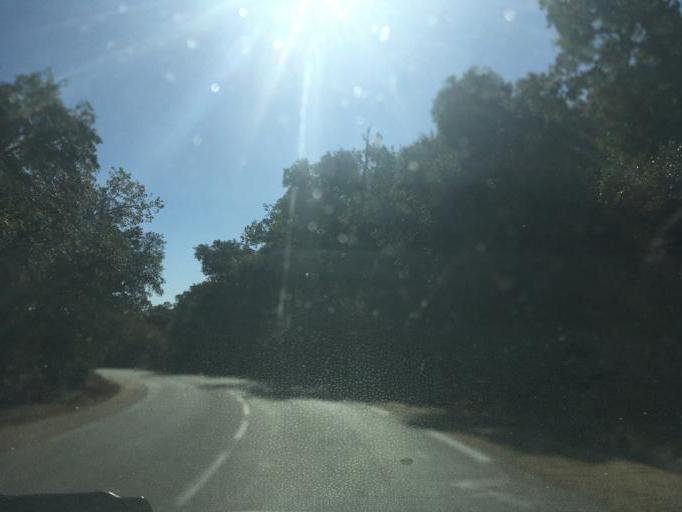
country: FR
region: Provence-Alpes-Cote d'Azur
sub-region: Departement du Var
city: La Garde-Freinet
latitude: 43.2914
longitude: 6.4921
